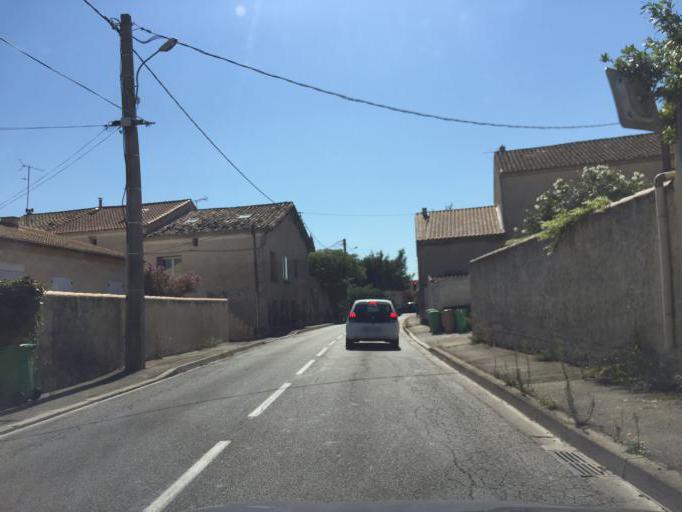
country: FR
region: Provence-Alpes-Cote d'Azur
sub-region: Departement du Vaucluse
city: Saint-Saturnin-les-Avignon
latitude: 43.9605
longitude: 4.9323
